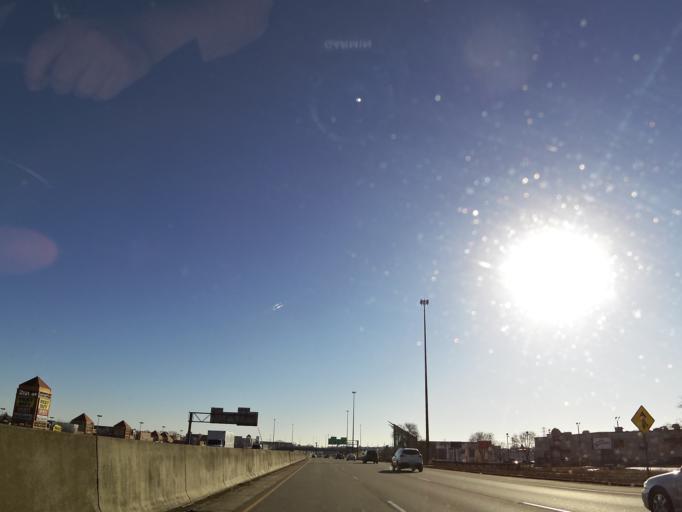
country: US
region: Minnesota
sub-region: Hennepin County
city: Bloomington
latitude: 44.8618
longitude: -93.2962
